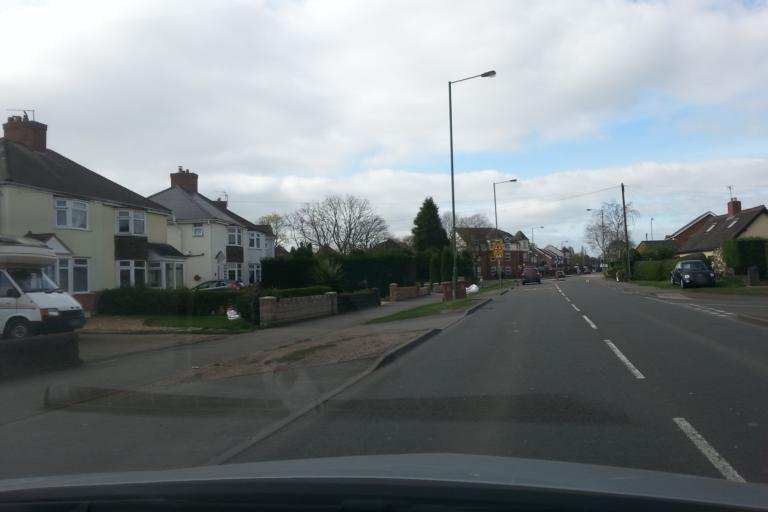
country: GB
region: England
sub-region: Walsall
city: Aldridge
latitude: 52.5996
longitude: -1.9236
